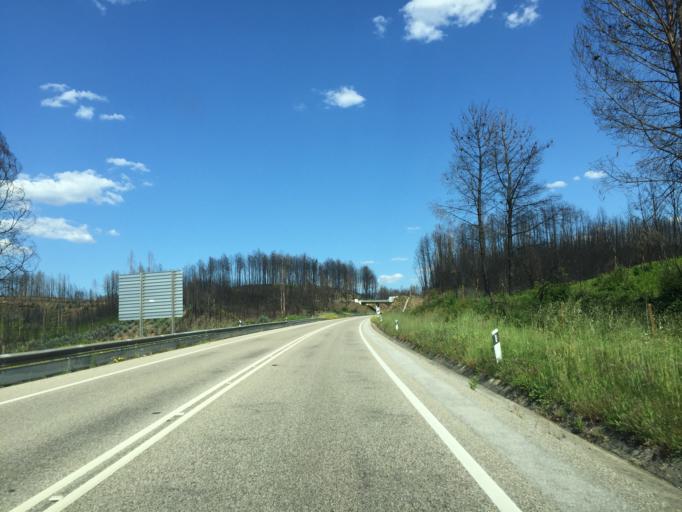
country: PT
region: Leiria
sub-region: Pedrogao Grande
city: Pedrogao Grande
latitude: 39.9279
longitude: -8.1855
